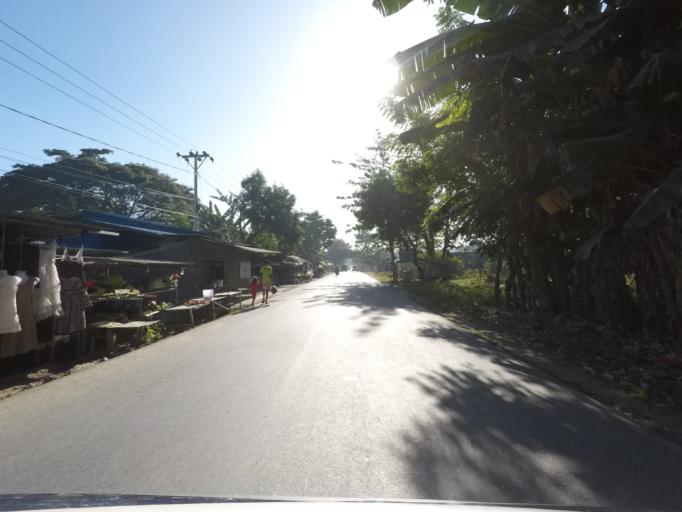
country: ID
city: Metinaro
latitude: -8.5490
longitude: 125.6651
